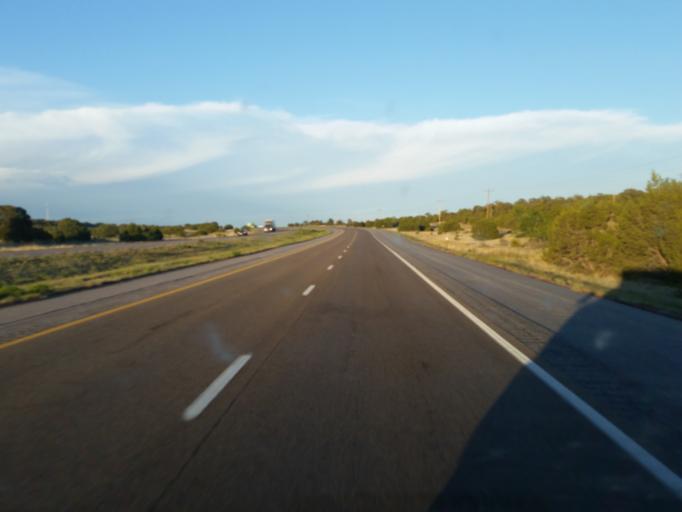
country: US
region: New Mexico
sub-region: Torrance County
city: Moriarty
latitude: 35.0020
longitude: -105.5576
